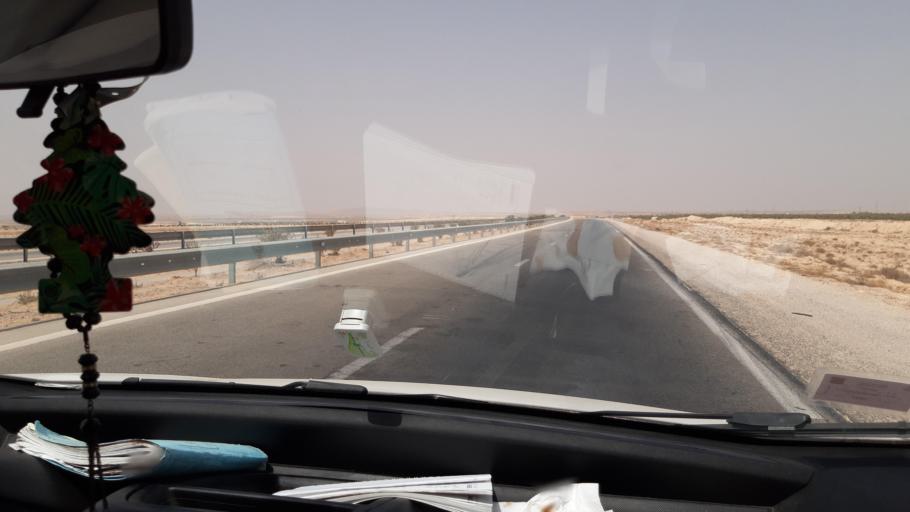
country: TN
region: Qabis
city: Gabes
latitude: 33.9505
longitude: 9.9581
